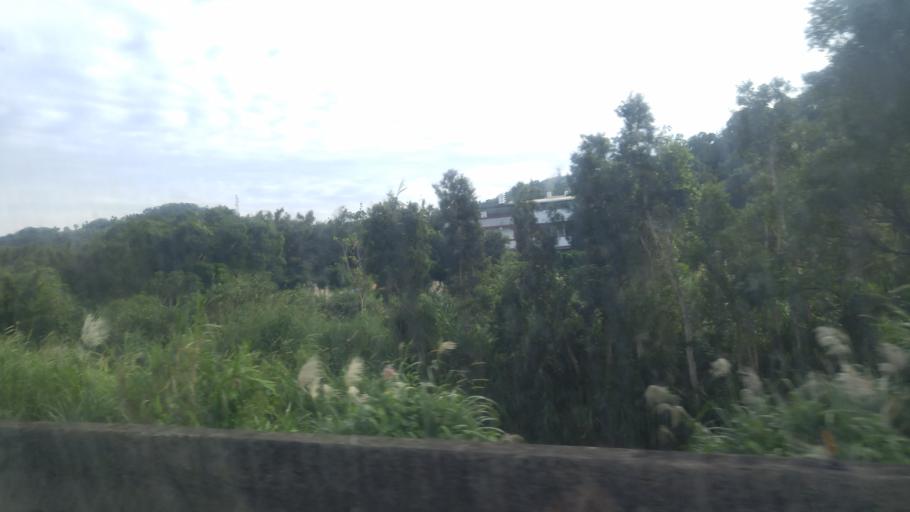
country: TW
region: Taiwan
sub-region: Hsinchu
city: Zhubei
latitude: 24.8929
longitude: 121.1187
